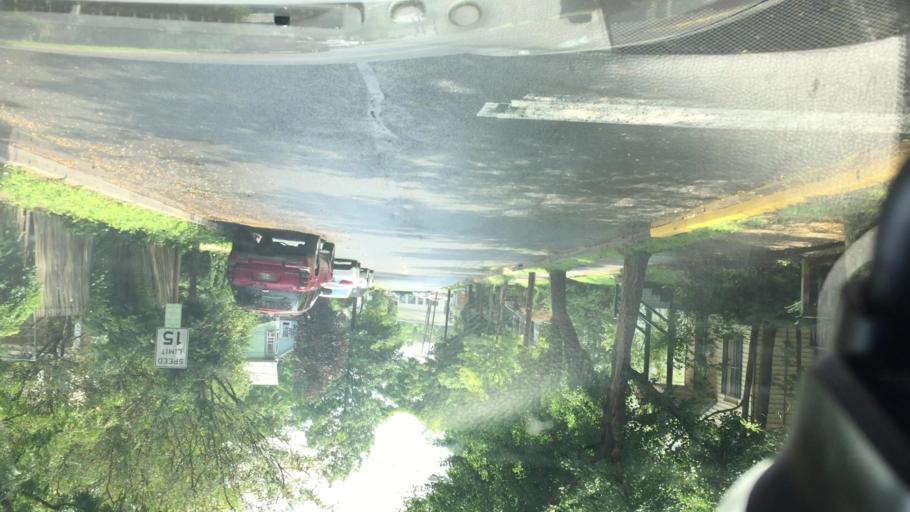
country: US
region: Pennsylvania
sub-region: Monroe County
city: Stroudsburg
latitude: 40.9877
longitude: -75.2009
